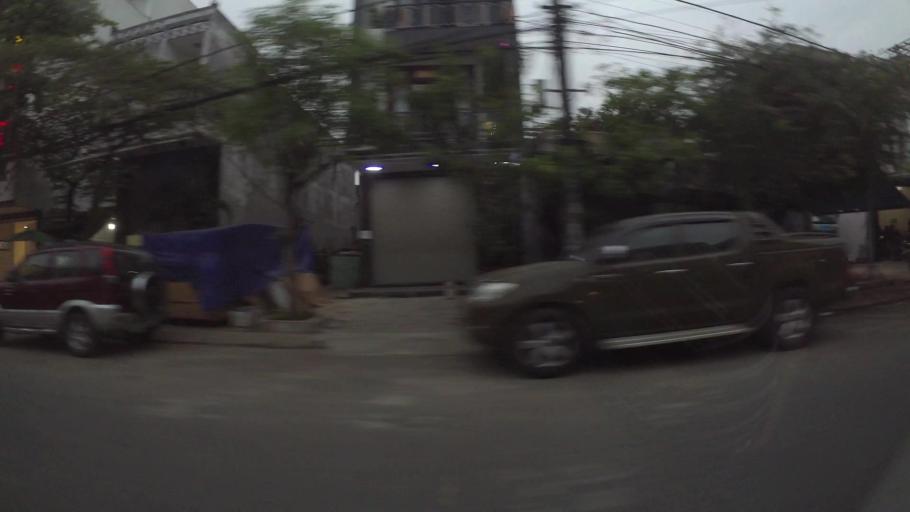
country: VN
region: Da Nang
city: Lien Chieu
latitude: 16.0542
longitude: 108.1715
